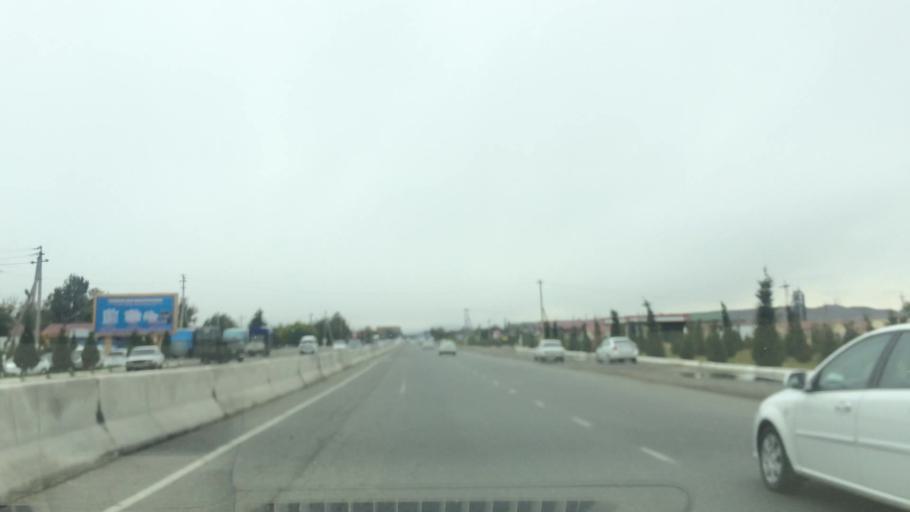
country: UZ
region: Samarqand
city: Jomboy
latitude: 39.7034
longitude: 67.0793
